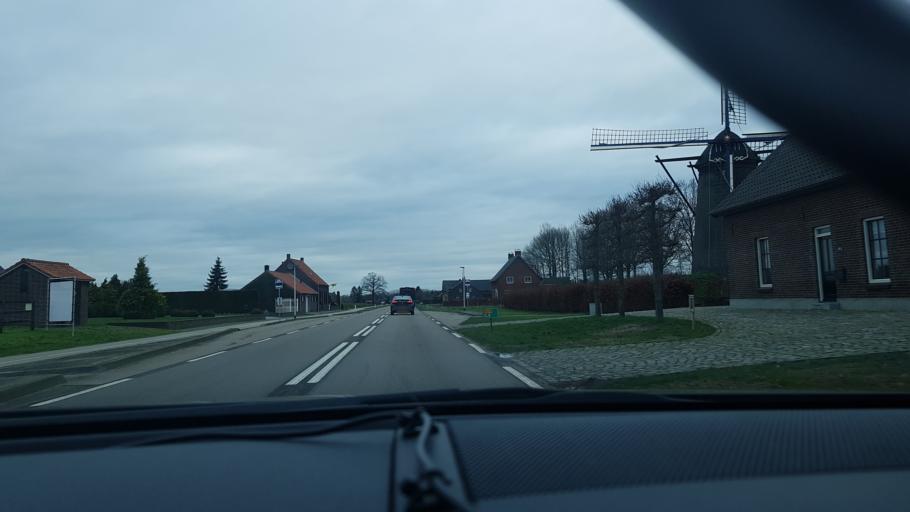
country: NL
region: Limburg
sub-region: Gemeente Leudal
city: Heythuysen
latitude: 51.2788
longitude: 5.9117
